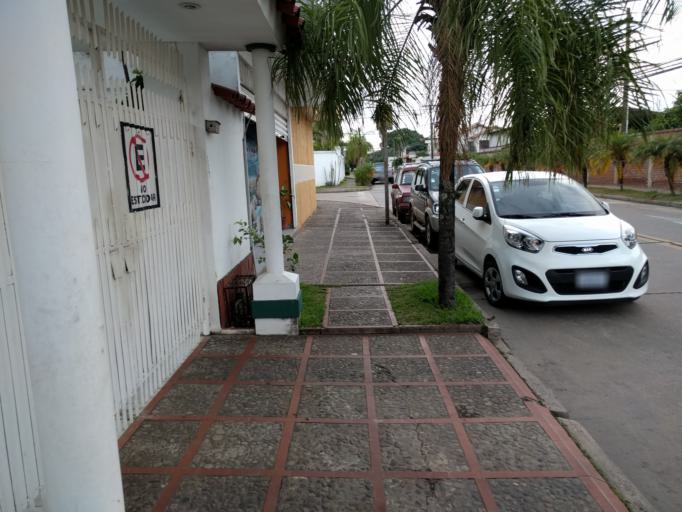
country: BO
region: Santa Cruz
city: Santa Cruz de la Sierra
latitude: -17.8085
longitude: -63.2052
